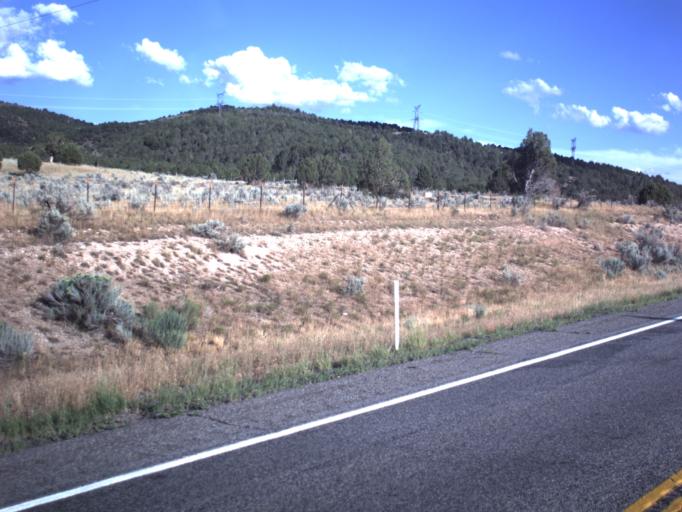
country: US
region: Utah
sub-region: Utah County
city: Woodland Hills
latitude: 39.8943
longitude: -111.5500
